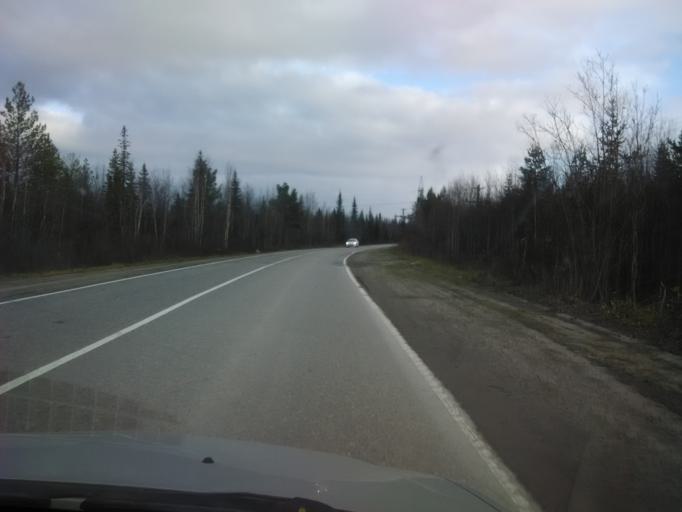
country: RU
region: Murmansk
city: Polyarnyye Zori
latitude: 67.3868
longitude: 32.5163
